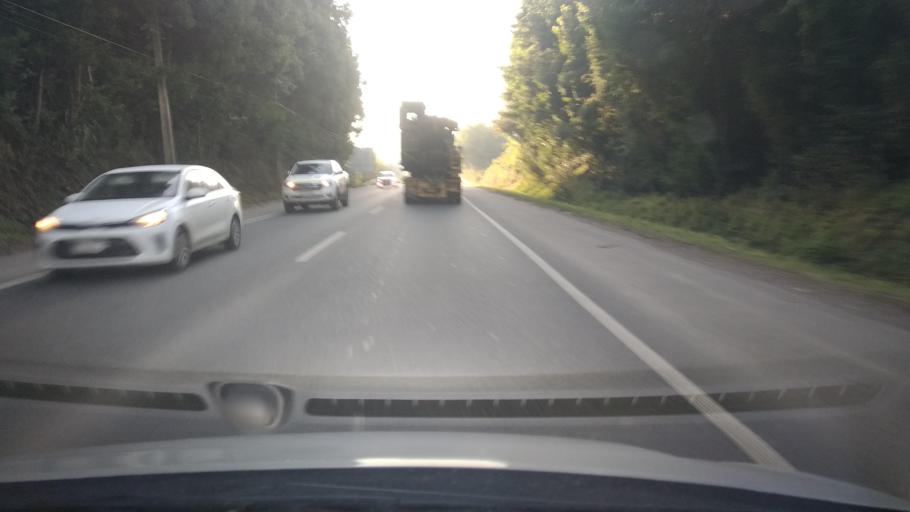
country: CL
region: Los Lagos
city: Las Animas
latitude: -39.7825
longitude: -73.2142
